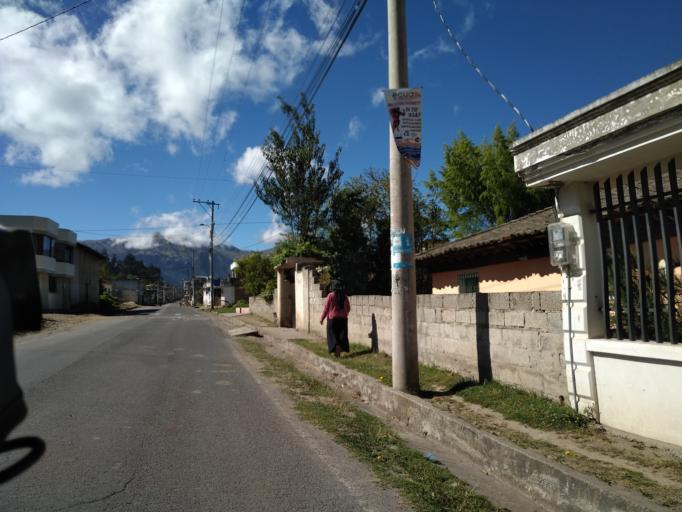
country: EC
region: Imbabura
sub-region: Canton Otavalo
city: Otavalo
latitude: 0.2164
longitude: -78.2155
